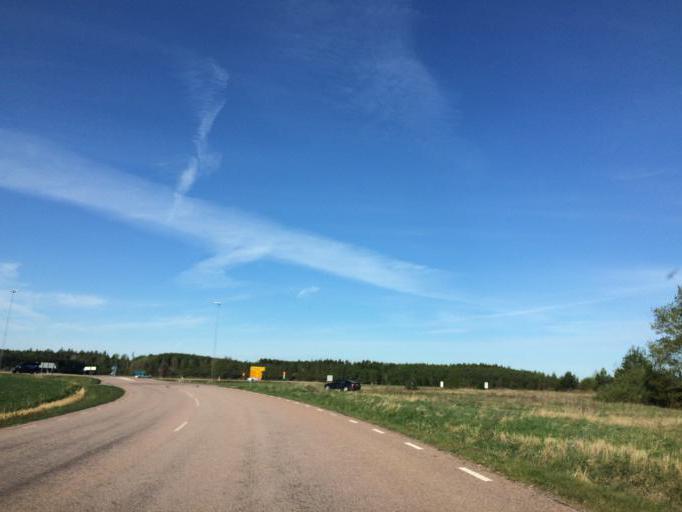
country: SE
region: Soedermanland
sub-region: Eskilstuna Kommun
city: Kvicksund
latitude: 59.4085
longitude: 16.2477
